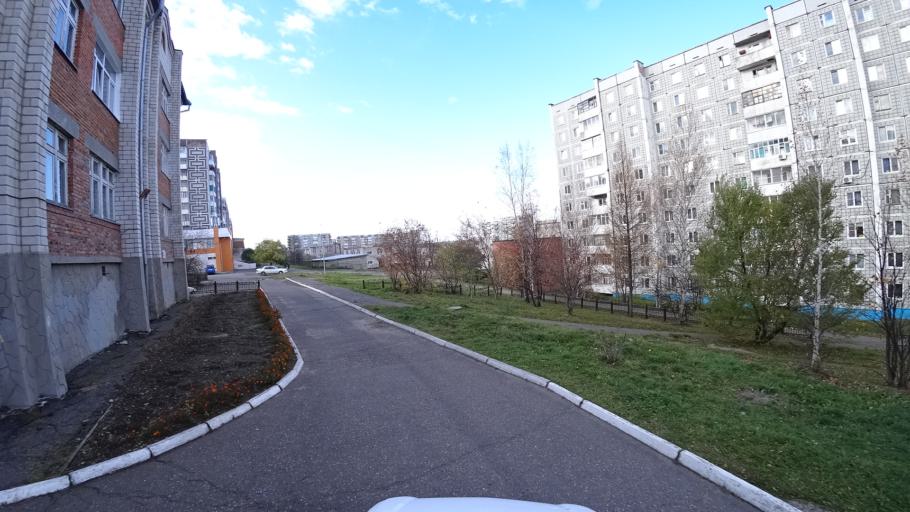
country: RU
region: Khabarovsk Krai
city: Amursk
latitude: 50.2468
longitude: 136.9197
